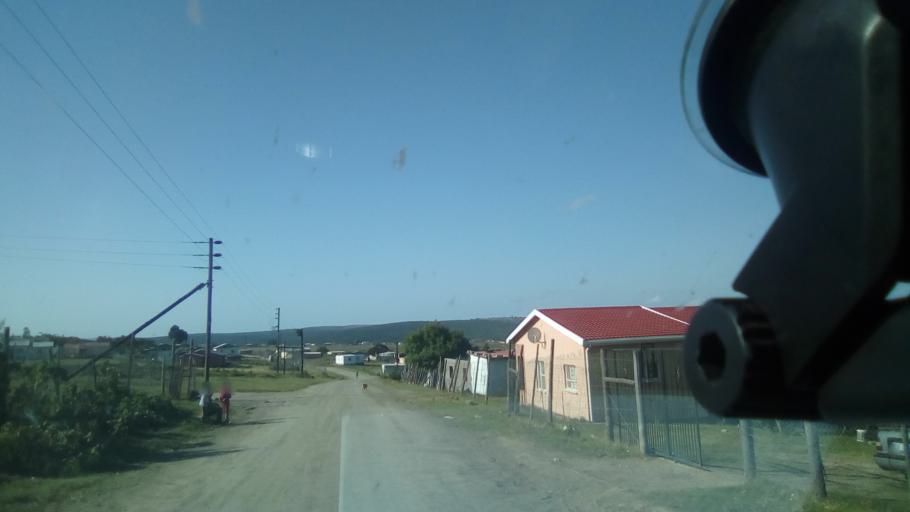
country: ZA
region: Eastern Cape
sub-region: Buffalo City Metropolitan Municipality
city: Bhisho
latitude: -32.8139
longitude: 27.3534
